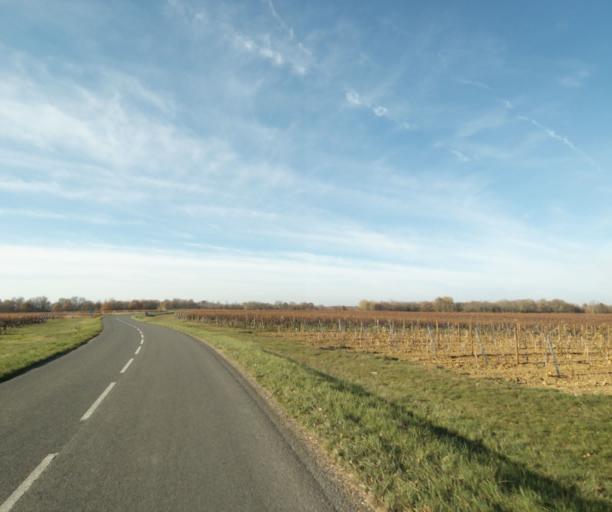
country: FR
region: Poitou-Charentes
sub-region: Departement de la Charente-Maritime
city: Burie
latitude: 45.7684
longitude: -0.4378
